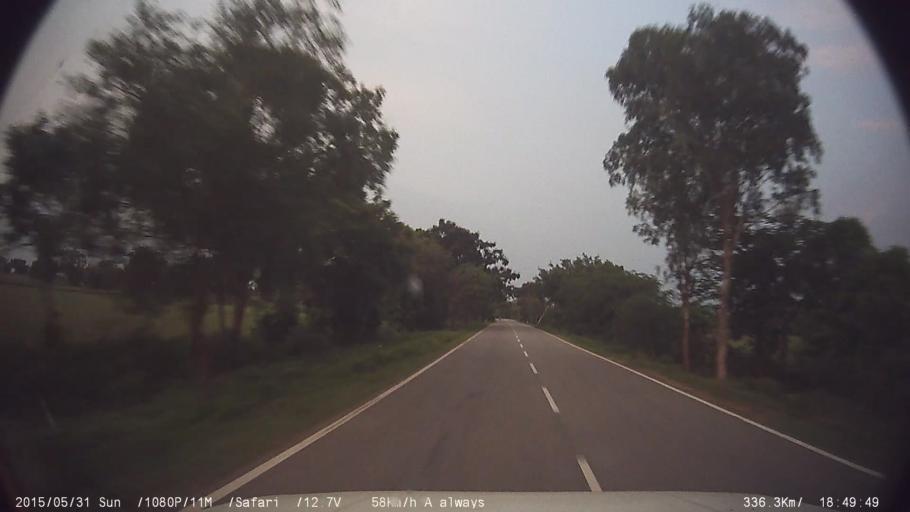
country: IN
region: Karnataka
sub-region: Mysore
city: Tirumakudal Narsipur
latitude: 12.1751
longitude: 76.8533
